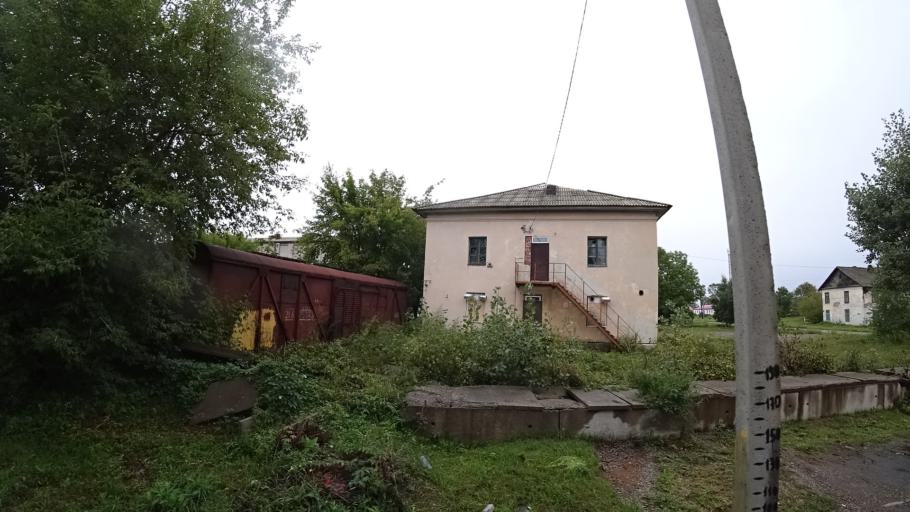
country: RU
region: Primorskiy
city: Monastyrishche
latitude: 44.1953
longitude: 132.4240
